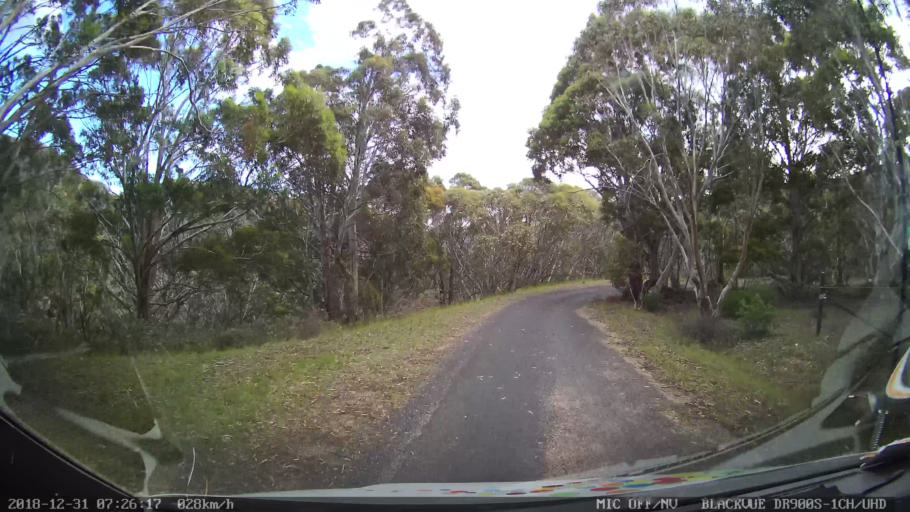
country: AU
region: New South Wales
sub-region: Snowy River
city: Jindabyne
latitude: -36.3184
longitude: 148.4804
